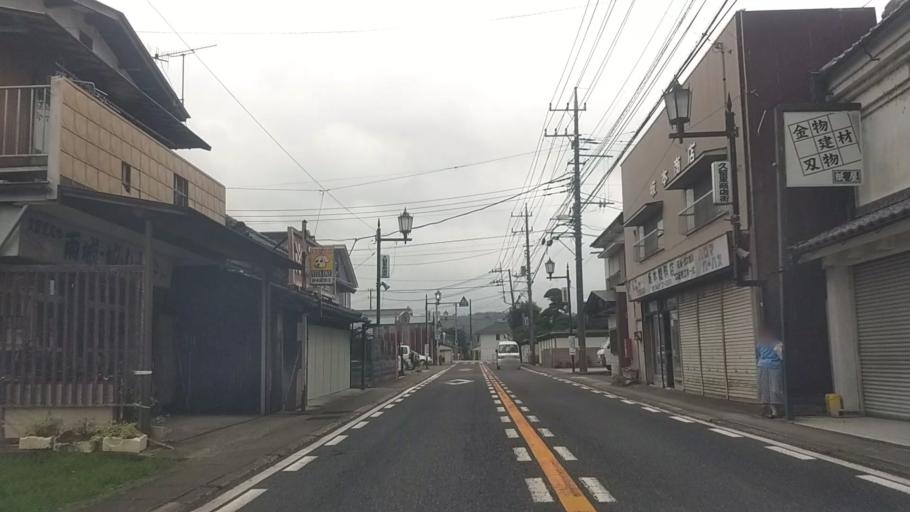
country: JP
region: Chiba
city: Kisarazu
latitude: 35.2944
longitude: 140.0784
